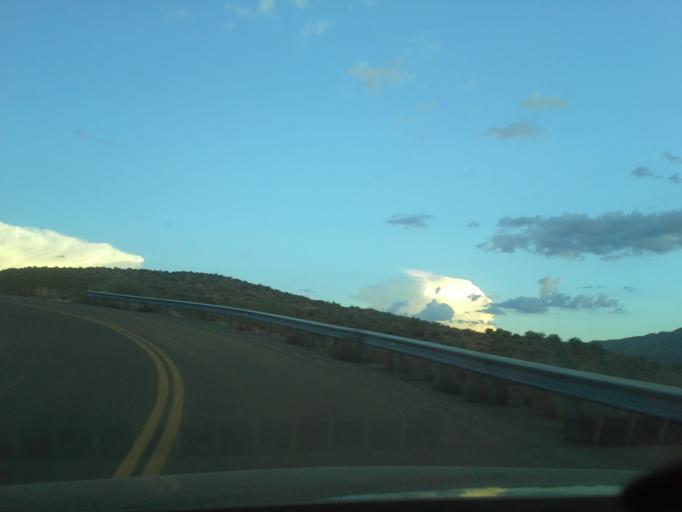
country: US
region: Arizona
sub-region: Yavapai County
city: Black Canyon City
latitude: 34.1534
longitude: -112.1564
